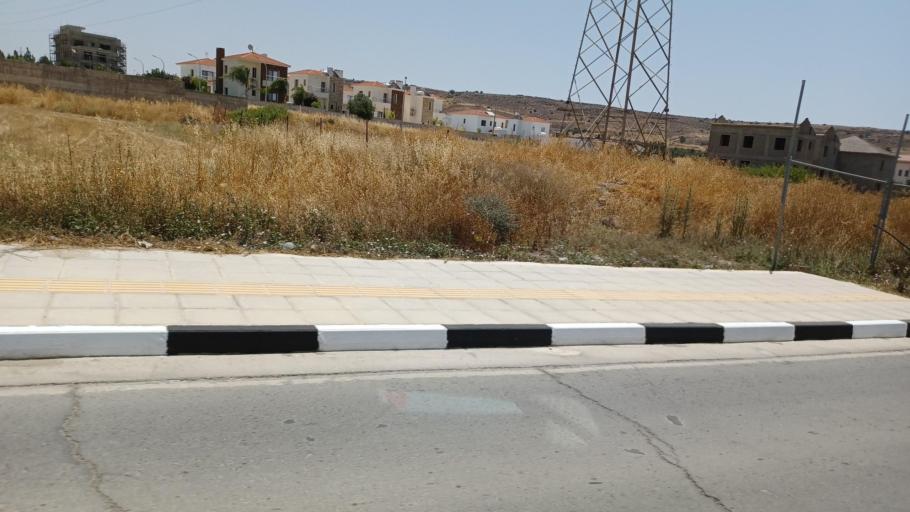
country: CY
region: Larnaka
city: Pyla
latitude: 34.9970
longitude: 33.6922
